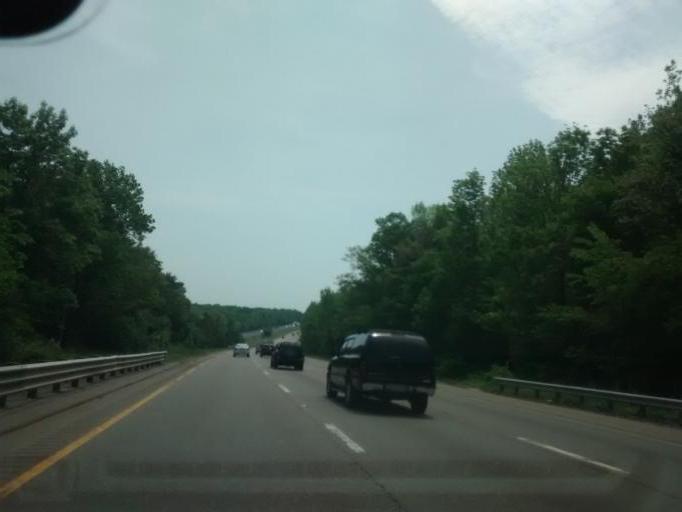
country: US
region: Massachusetts
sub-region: Norfolk County
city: Franklin
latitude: 42.0532
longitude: -71.3720
